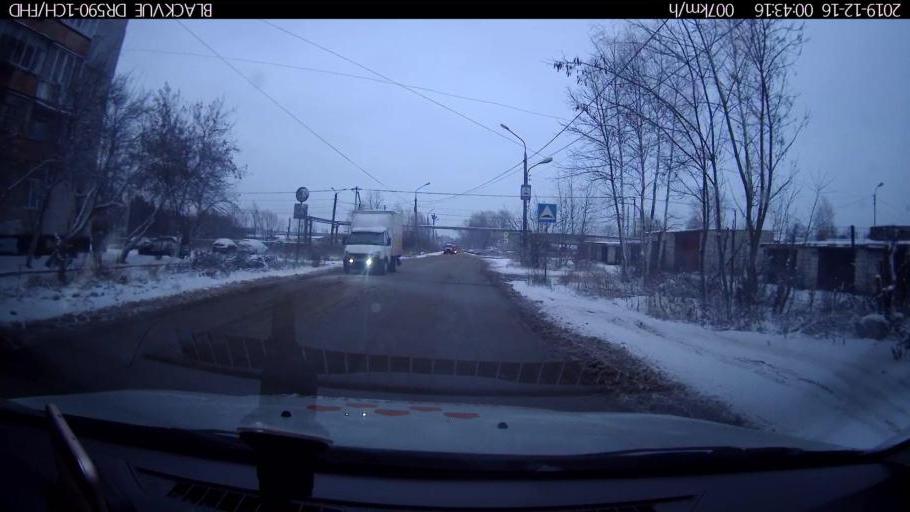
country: RU
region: Nizjnij Novgorod
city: Gorbatovka
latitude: 56.3004
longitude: 43.8532
